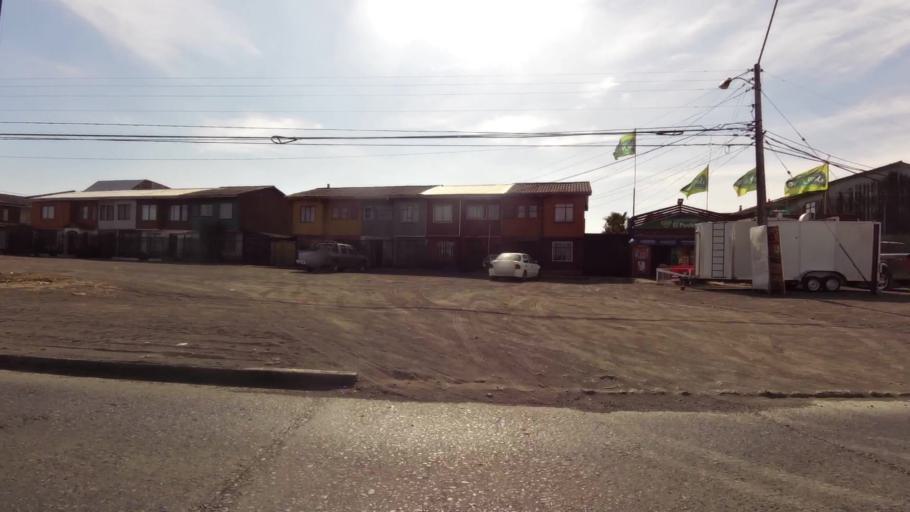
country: CL
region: Biobio
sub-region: Provincia de Concepcion
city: Talcahuano
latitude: -36.7865
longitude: -73.1102
